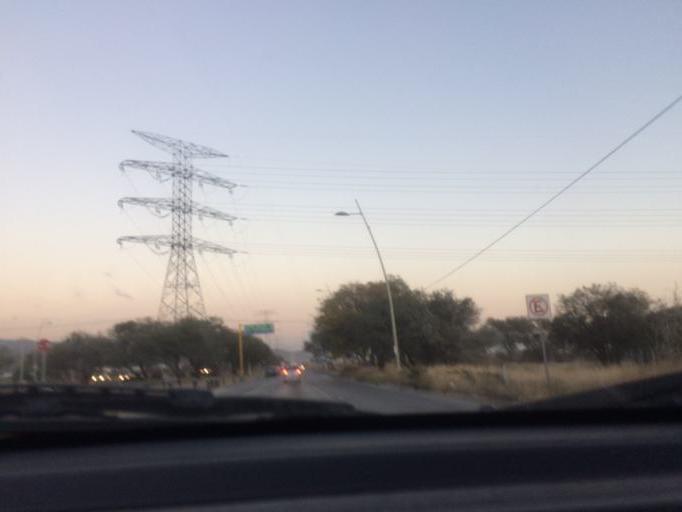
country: MX
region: Guanajuato
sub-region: Leon
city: Medina
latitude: 21.1378
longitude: -101.6222
